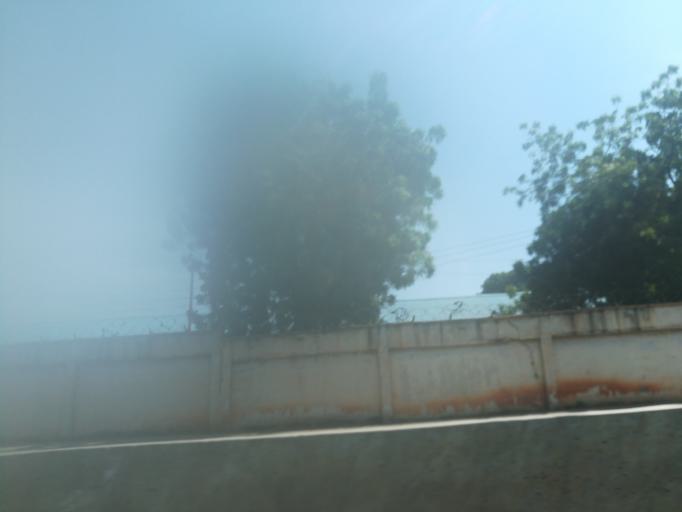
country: NG
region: Kano
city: Kano
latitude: 12.0372
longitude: 8.5255
